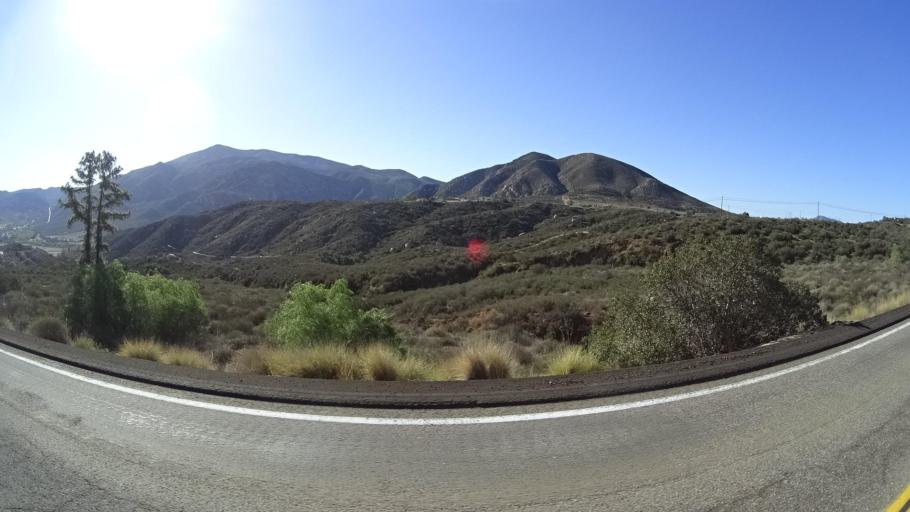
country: MX
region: Baja California
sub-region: Tijuana
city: Villa del Campo
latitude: 32.6174
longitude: -116.7326
